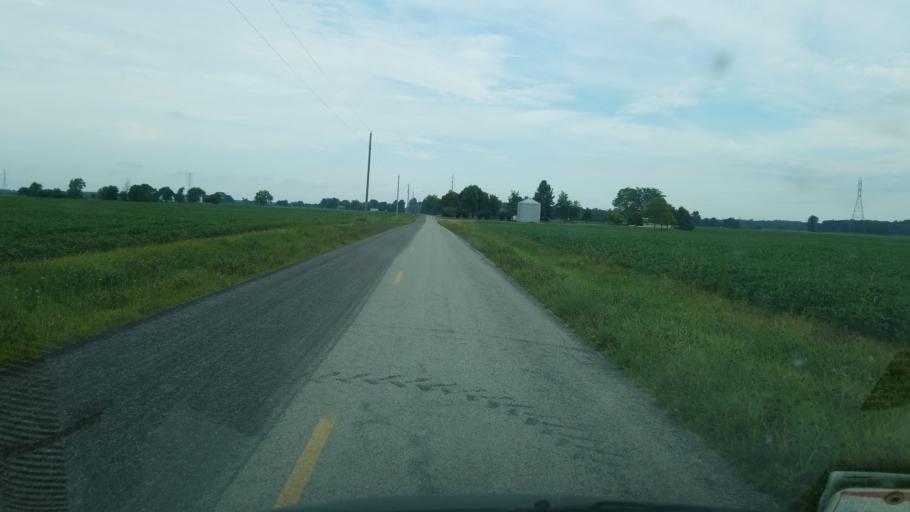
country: US
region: Ohio
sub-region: Seneca County
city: Tiffin
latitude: 41.0030
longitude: -83.0549
